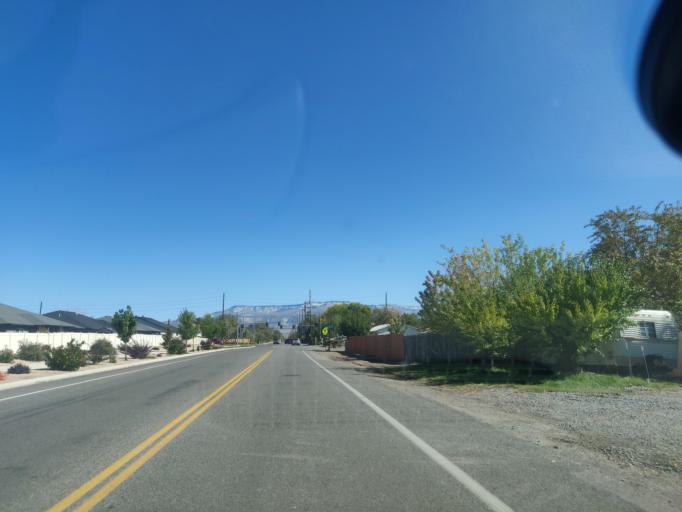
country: US
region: Colorado
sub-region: Mesa County
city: Fruitvale
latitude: 39.0699
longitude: -108.4987
